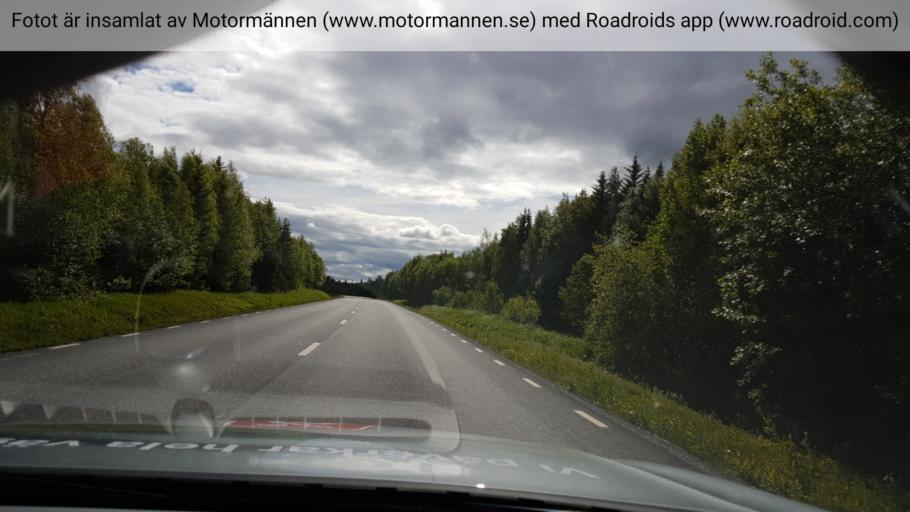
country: SE
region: Jaemtland
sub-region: Stroemsunds Kommun
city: Stroemsund
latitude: 64.1227
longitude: 15.6320
